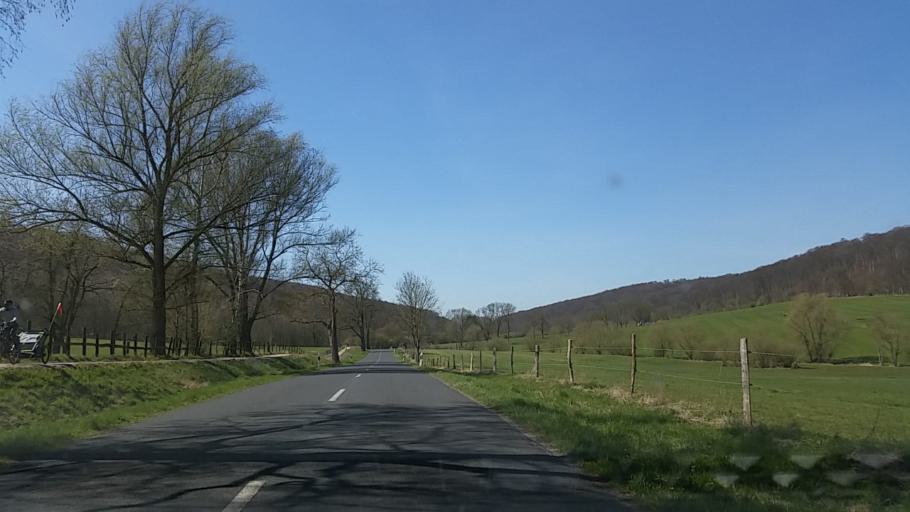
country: DE
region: Lower Saxony
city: Kneitlingen
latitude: 52.2076
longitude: 10.7538
